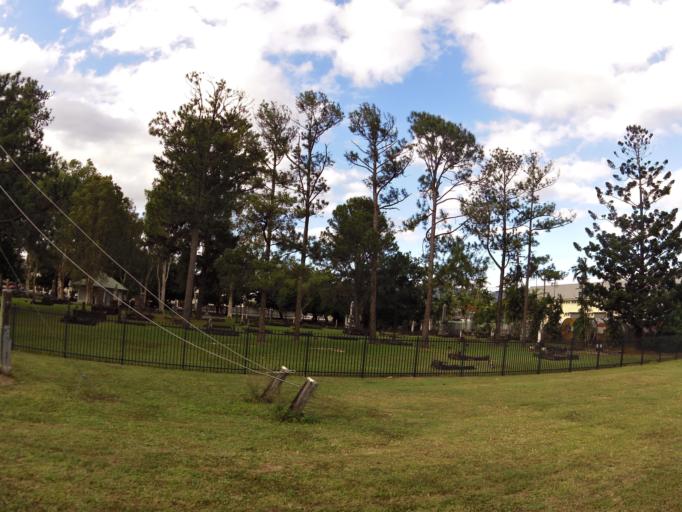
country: AU
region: Queensland
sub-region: Cairns
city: Cairns
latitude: -16.9164
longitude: 145.7642
